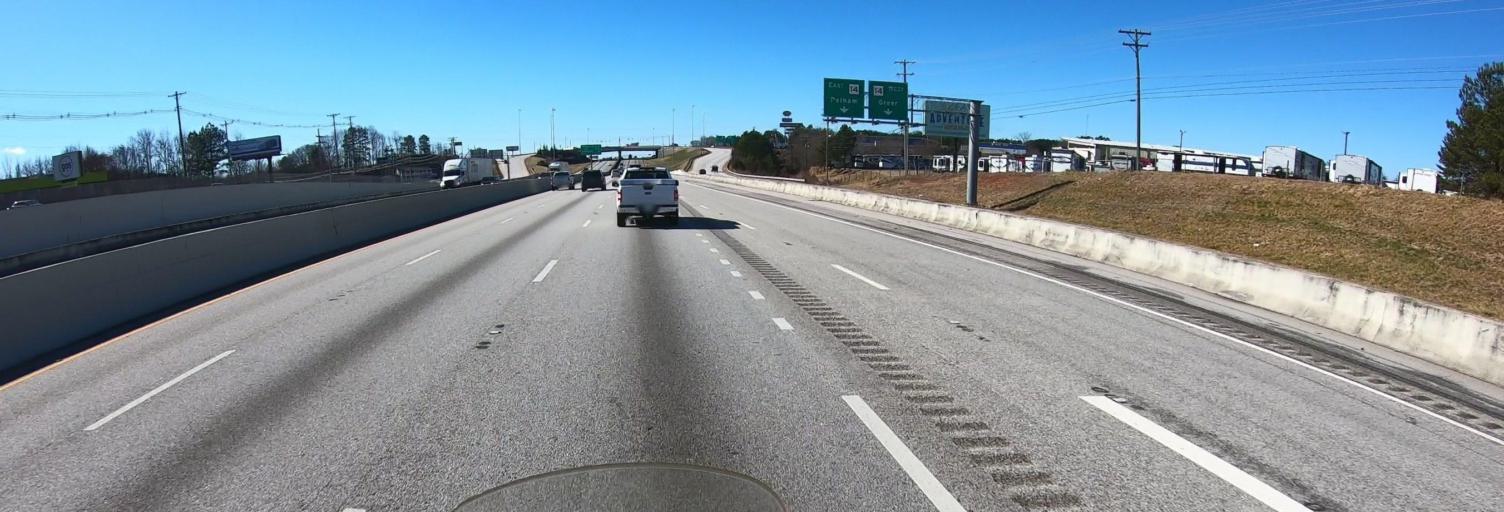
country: US
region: South Carolina
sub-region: Greenville County
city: Greer
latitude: 34.8741
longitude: -82.2214
